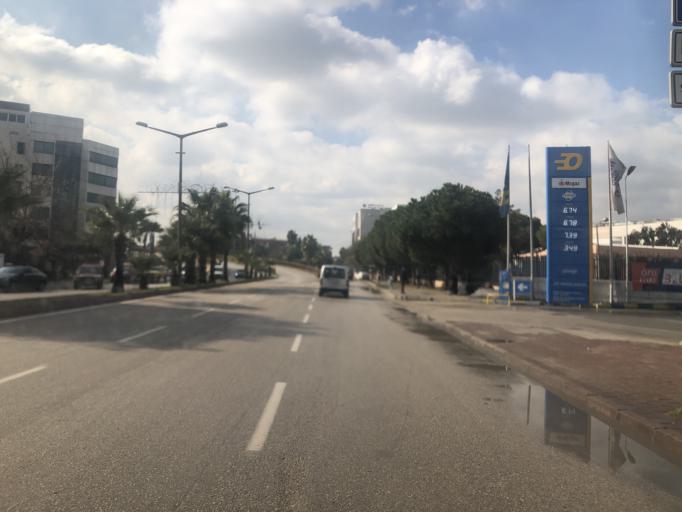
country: TR
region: Adana
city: Adana
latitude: 36.9908
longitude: 35.3452
